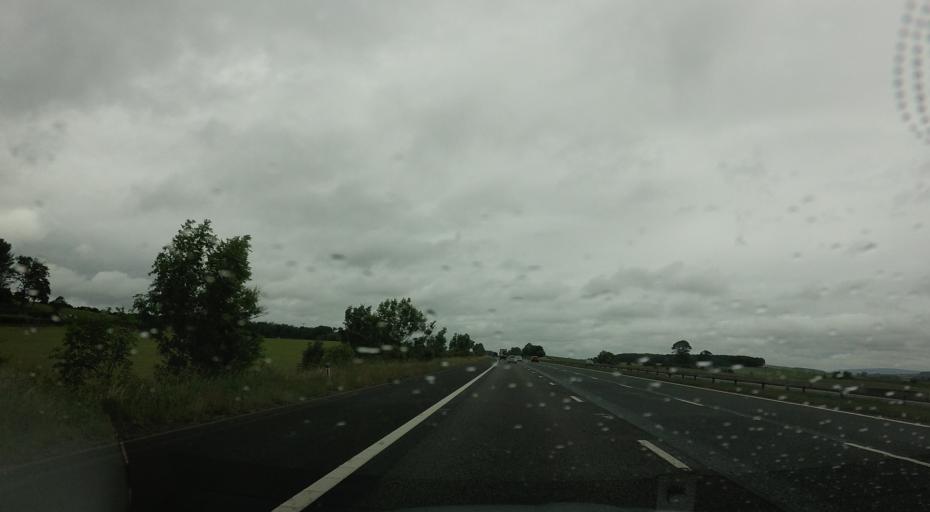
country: GB
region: England
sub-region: Cumbria
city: Penrith
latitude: 54.7290
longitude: -2.8025
